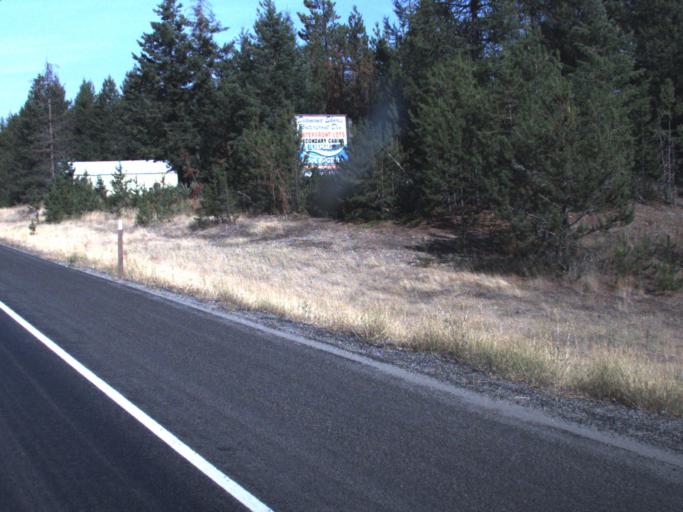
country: US
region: Washington
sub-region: Pend Oreille County
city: Newport
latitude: 48.1262
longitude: -117.1879
